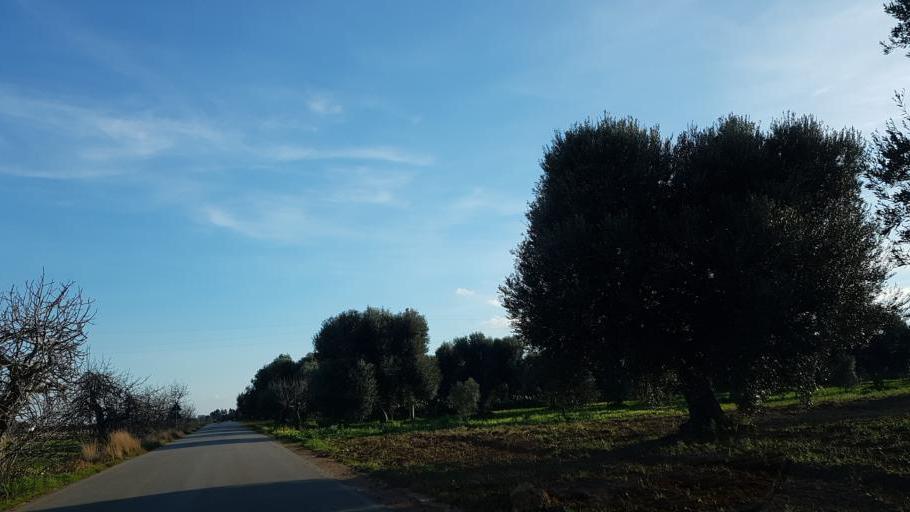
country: IT
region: Apulia
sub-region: Provincia di Brindisi
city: San Vito dei Normanni
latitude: 40.6889
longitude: 17.7644
